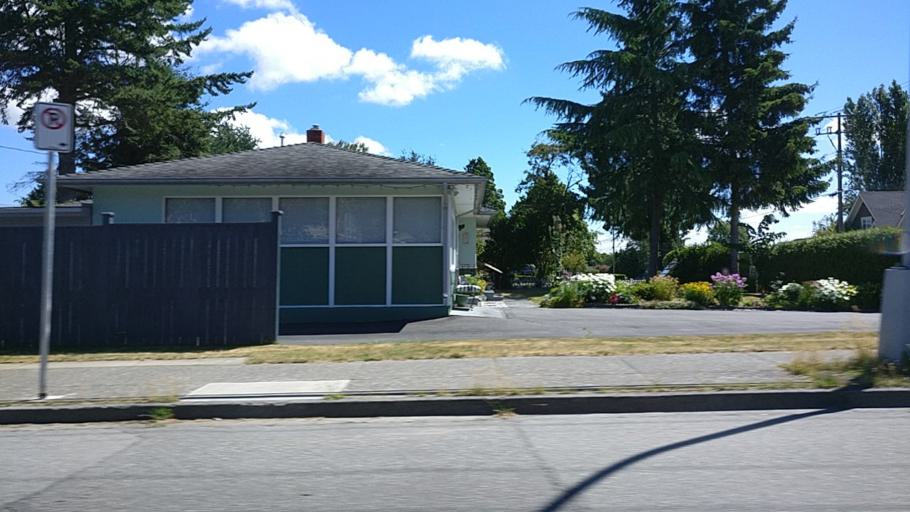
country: CA
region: British Columbia
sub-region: Greater Vancouver Regional District
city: White Rock
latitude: 49.0340
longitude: -122.7957
